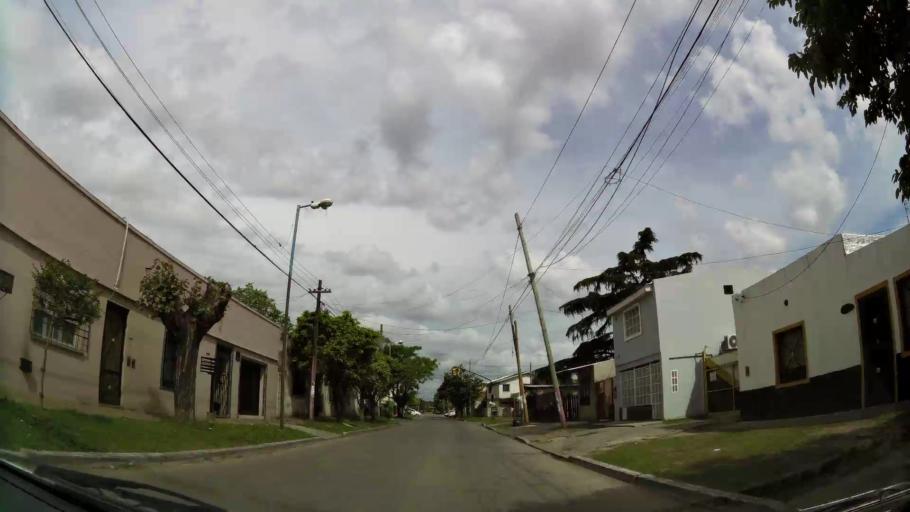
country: AR
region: Buenos Aires
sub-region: Partido de Quilmes
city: Quilmes
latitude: -34.7492
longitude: -58.2451
